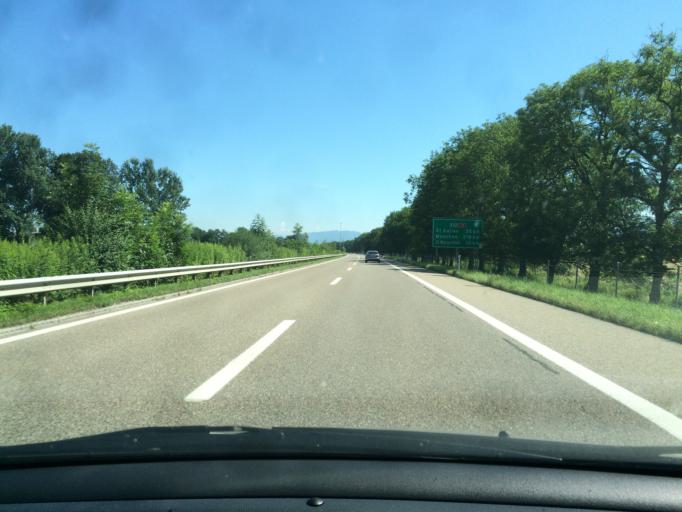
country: AT
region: Vorarlberg
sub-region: Politischer Bezirk Feldkirch
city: Mader
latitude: 47.3705
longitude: 9.6262
